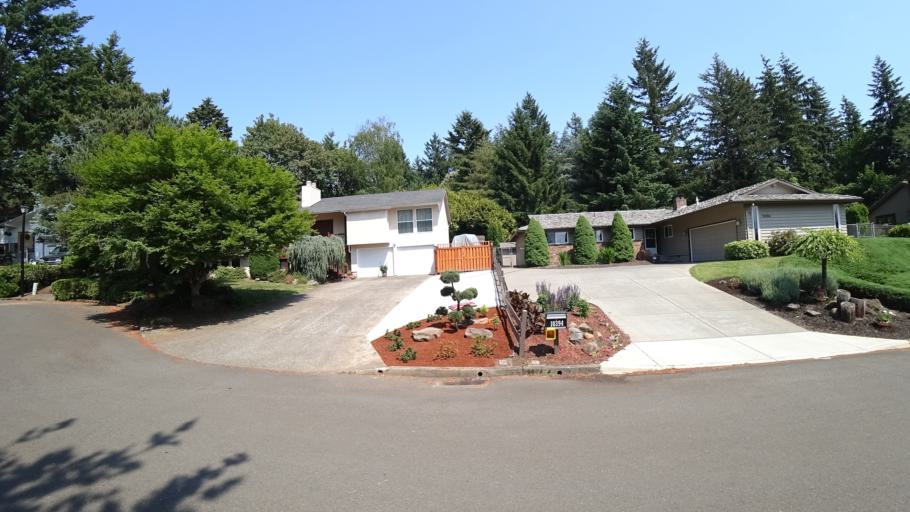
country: US
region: Oregon
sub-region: Multnomah County
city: Lents
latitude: 45.4481
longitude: -122.5630
